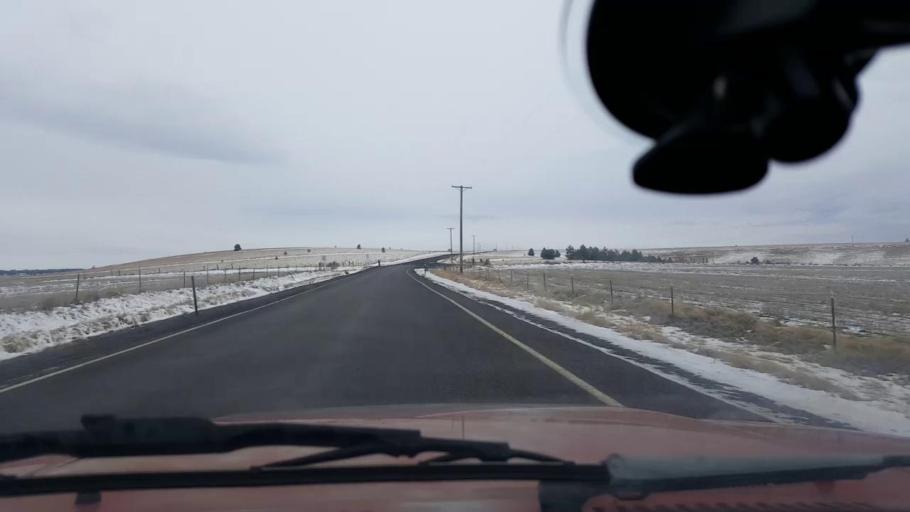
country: US
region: Washington
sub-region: Garfield County
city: Pomeroy
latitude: 46.3197
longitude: -117.3971
